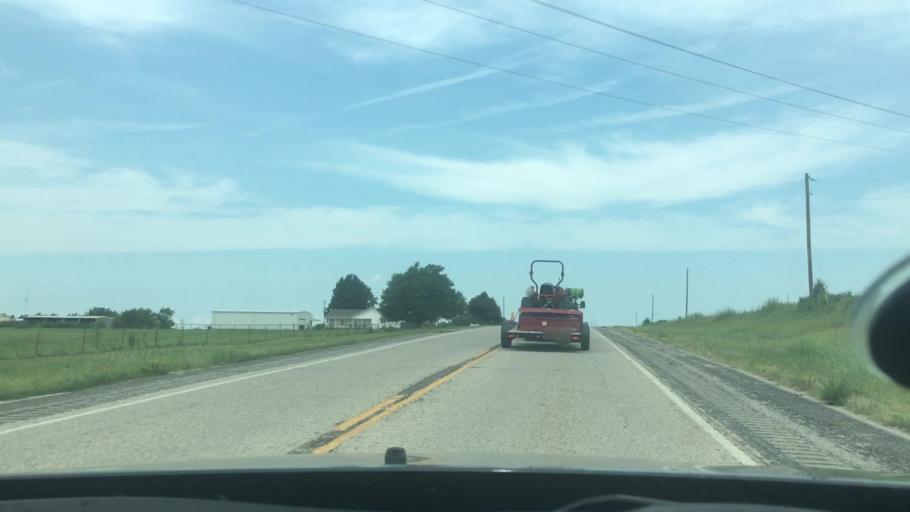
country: US
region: Oklahoma
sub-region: Seminole County
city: Seminole
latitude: 35.2756
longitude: -96.7240
